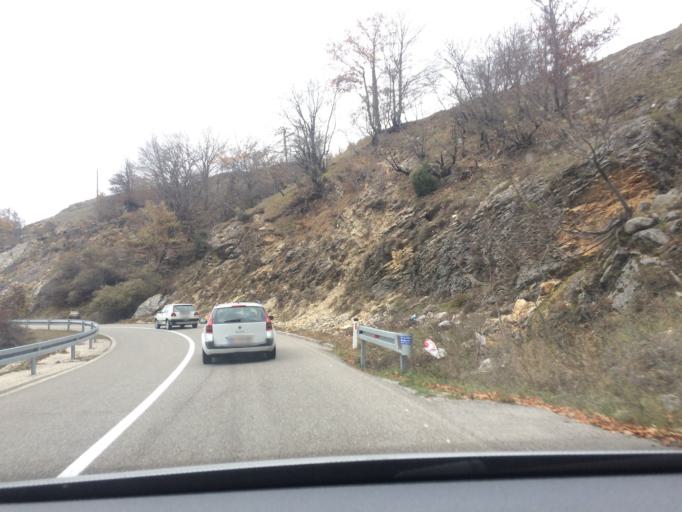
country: ME
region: Opstina Savnik
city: Savnik
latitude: 42.9501
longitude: 19.1000
